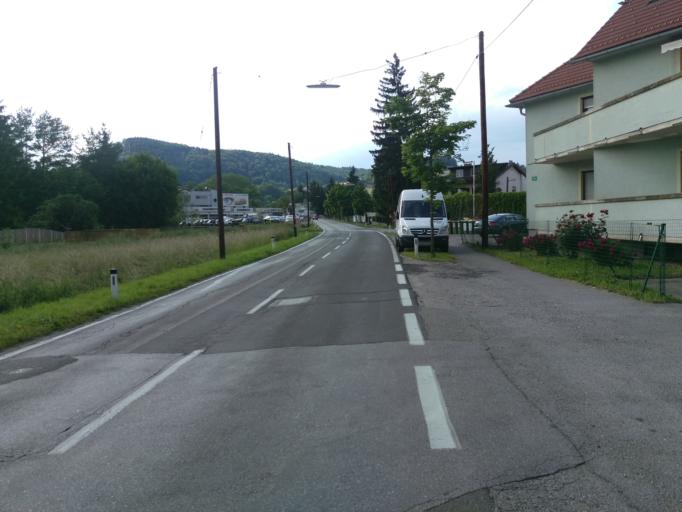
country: AT
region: Styria
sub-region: Graz Stadt
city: Goesting
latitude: 47.1087
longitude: 15.4164
